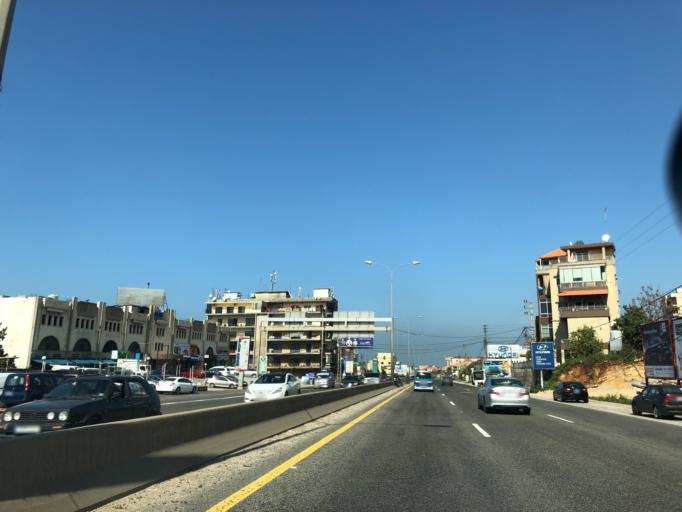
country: LB
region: Mont-Liban
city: Djounie
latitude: 34.0231
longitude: 35.6318
